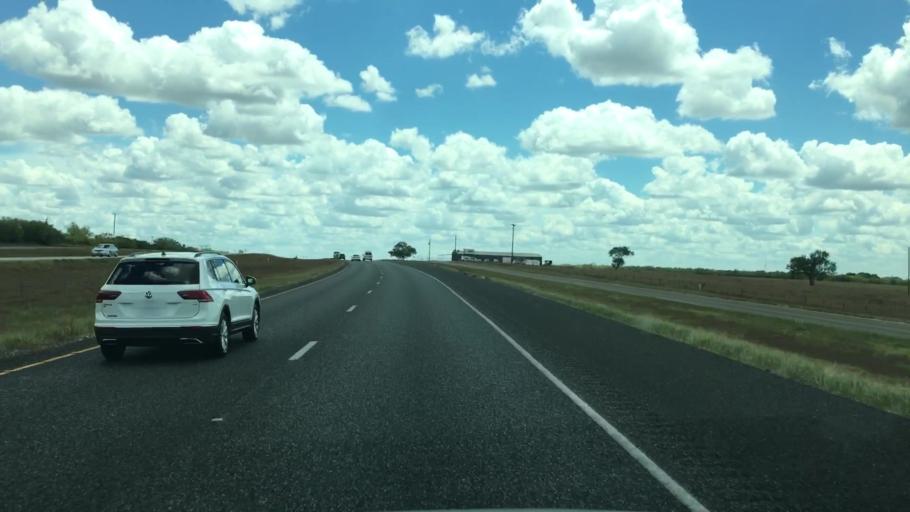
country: US
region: Texas
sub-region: Atascosa County
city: Pleasanton
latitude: 28.8720
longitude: -98.3959
